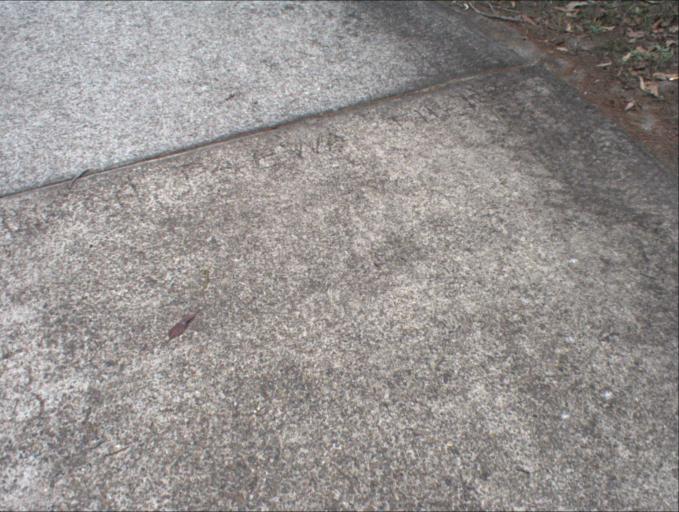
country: AU
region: Queensland
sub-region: Logan
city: Logan Reserve
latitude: -27.6912
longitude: 153.0783
